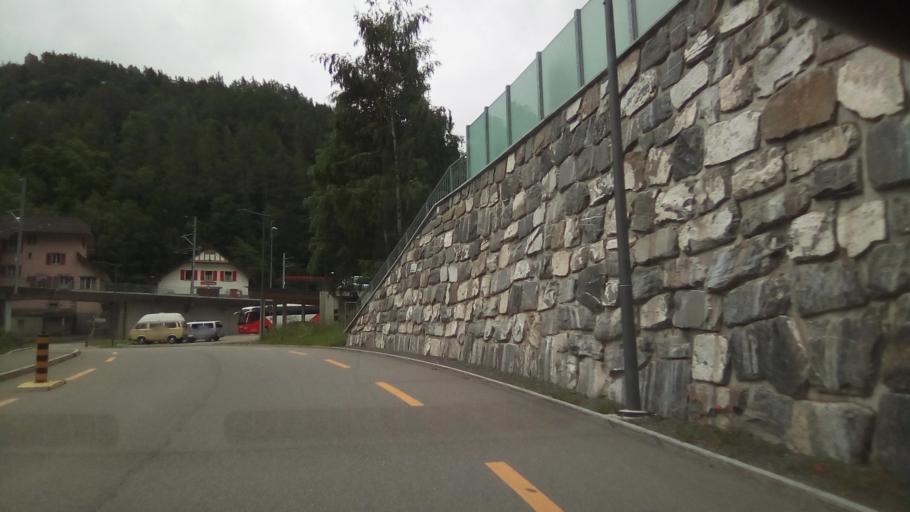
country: CH
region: Valais
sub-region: Martigny District
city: Charrat-les-Chenes
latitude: 46.0781
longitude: 7.1456
